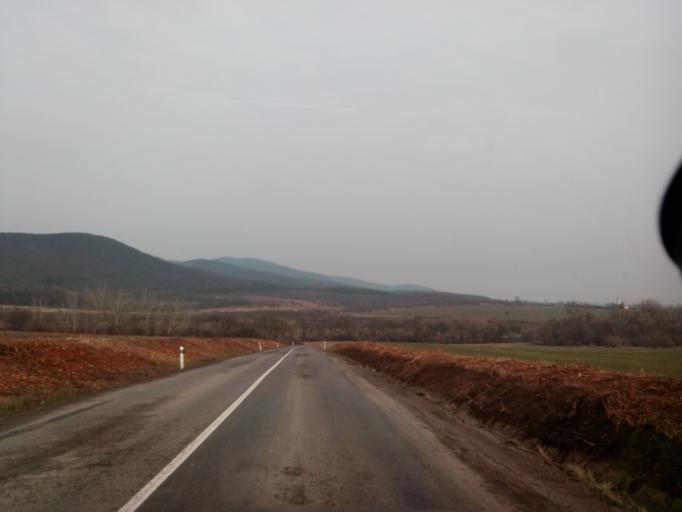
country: SK
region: Kosicky
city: Secovce
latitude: 48.6350
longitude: 21.5549
